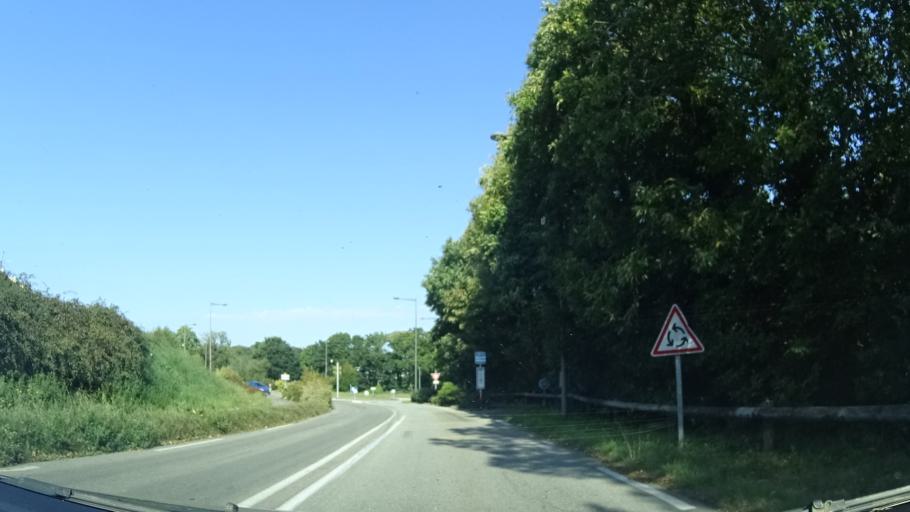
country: FR
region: Brittany
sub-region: Departement du Finistere
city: Douarnenez
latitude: 48.0855
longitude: -4.3347
